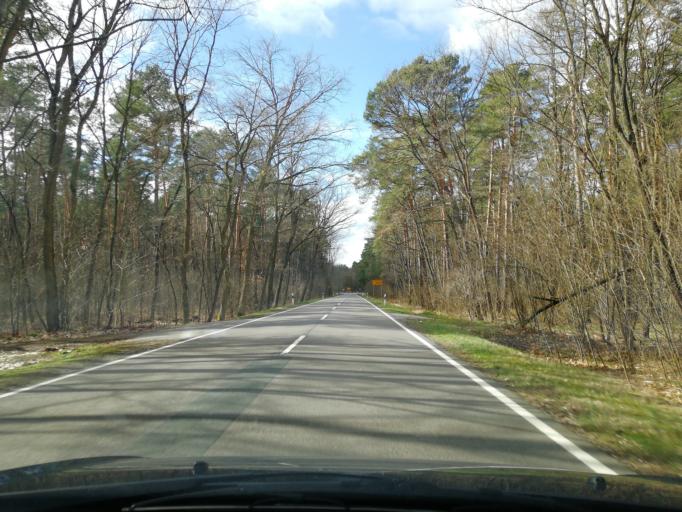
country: DE
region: Brandenburg
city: Altdobern
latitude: 51.7151
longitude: 14.0213
